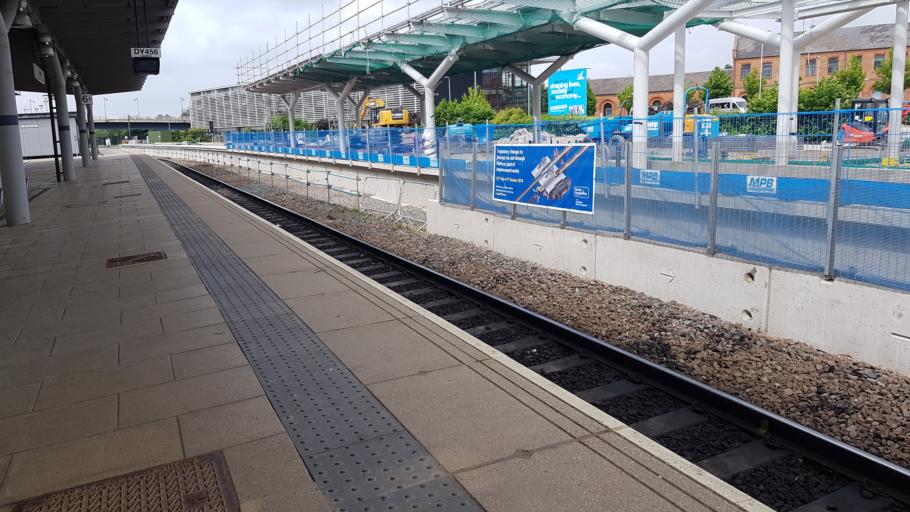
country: GB
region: England
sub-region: Derby
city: Derby
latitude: 52.9164
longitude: -1.4625
